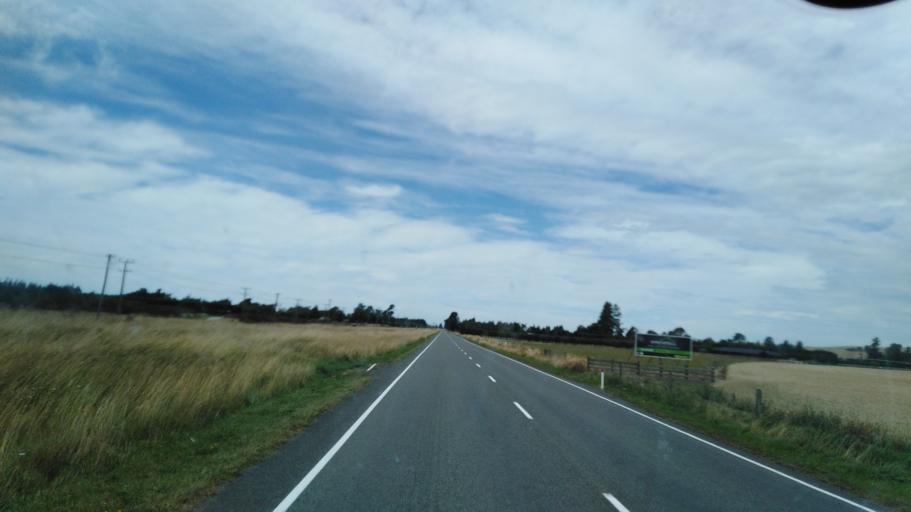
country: NZ
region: Canterbury
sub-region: Selwyn District
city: Darfield
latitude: -43.3694
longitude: 171.9854
